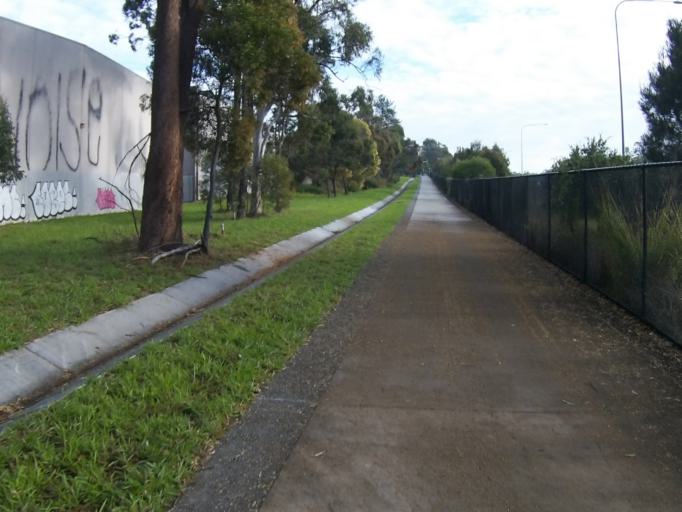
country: AU
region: Queensland
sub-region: Brisbane
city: Upper Mount Gravatt
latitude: -27.5787
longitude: 153.1012
